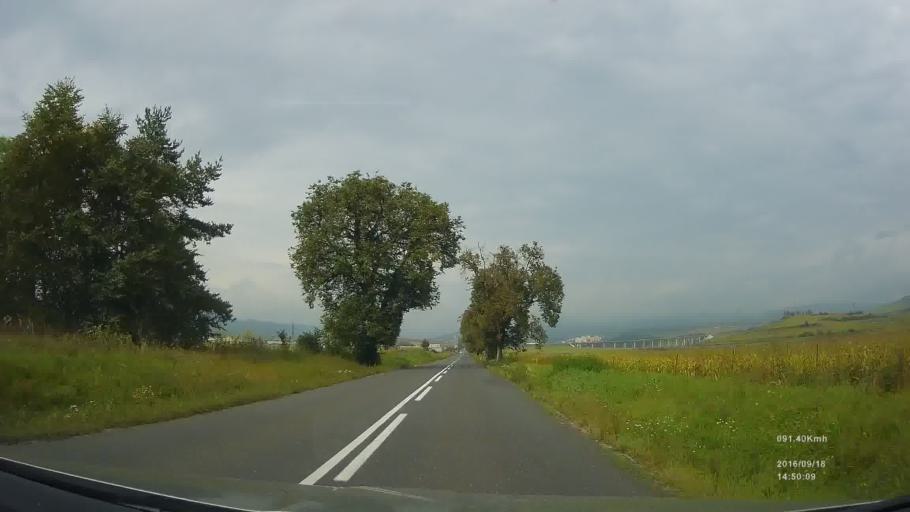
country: SK
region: Presovsky
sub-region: Okres Presov
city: Levoca
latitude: 48.9929
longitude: 20.5815
